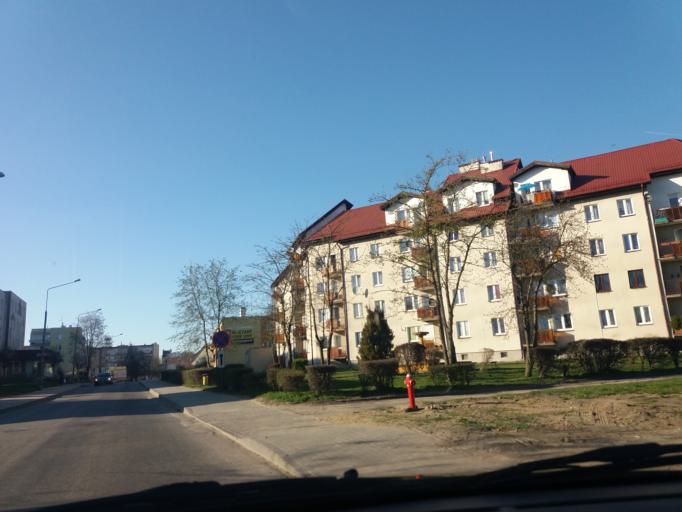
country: PL
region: Warmian-Masurian Voivodeship
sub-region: Powiat nidzicki
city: Nidzica
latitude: 53.3546
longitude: 20.4270
